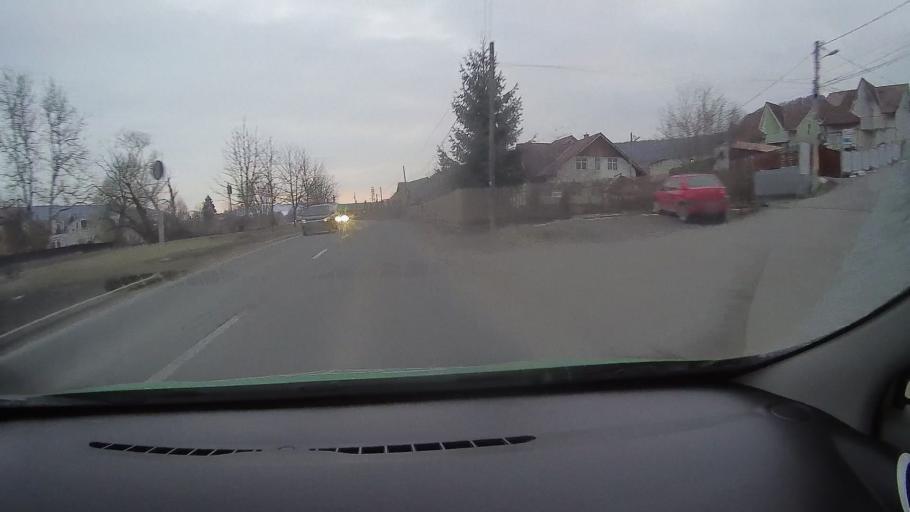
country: RO
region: Harghita
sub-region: Municipiul Odorheiu Secuiesc
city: Odorheiu Secuiesc
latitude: 46.3063
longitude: 25.2855
